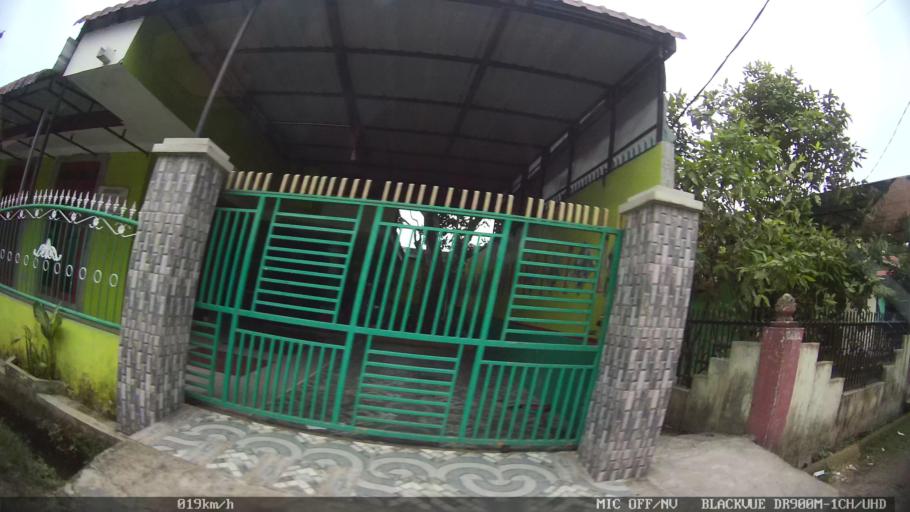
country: ID
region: North Sumatra
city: Medan
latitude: 3.5814
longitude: 98.7323
